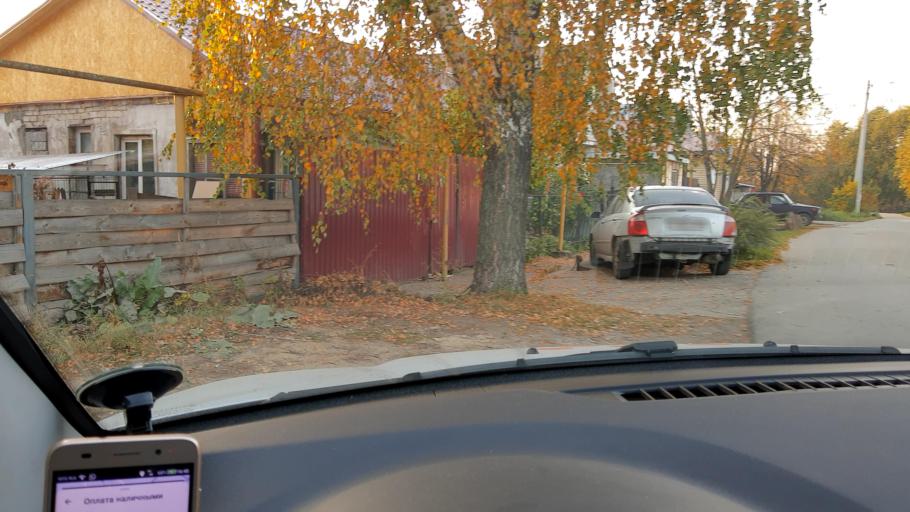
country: RU
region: Nizjnij Novgorod
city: Nizhniy Novgorod
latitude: 56.2800
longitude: 43.8866
